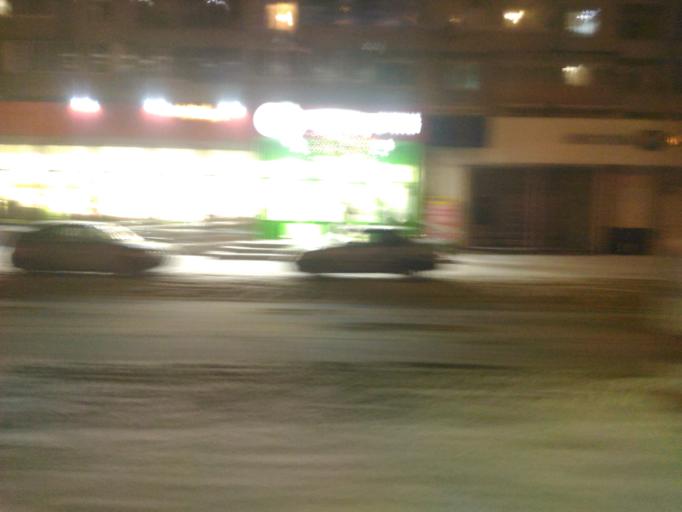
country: RU
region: Ulyanovsk
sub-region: Ulyanovskiy Rayon
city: Ulyanovsk
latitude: 54.3202
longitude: 48.3573
